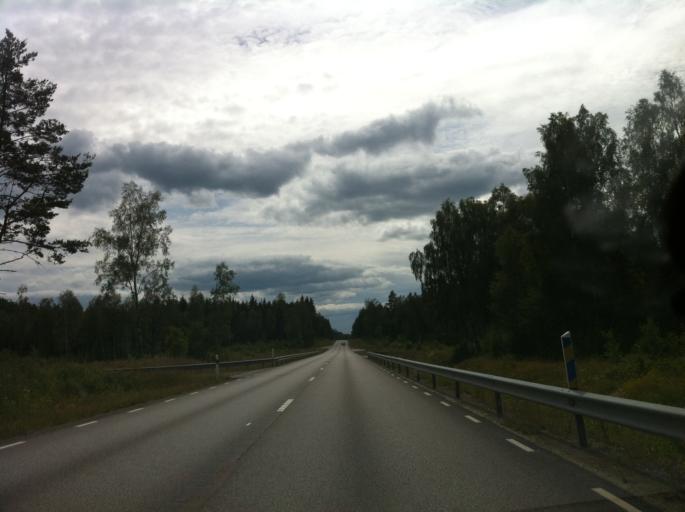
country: SE
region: Kronoberg
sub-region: Tingsryds Kommun
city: Tingsryd
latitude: 56.5239
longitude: 15.1675
